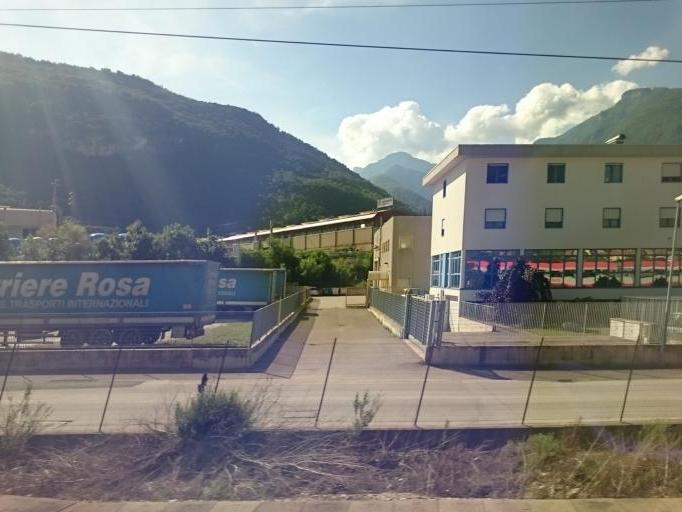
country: IT
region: Trentino-Alto Adige
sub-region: Provincia di Trento
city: Ala
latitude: 45.7679
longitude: 11.0070
